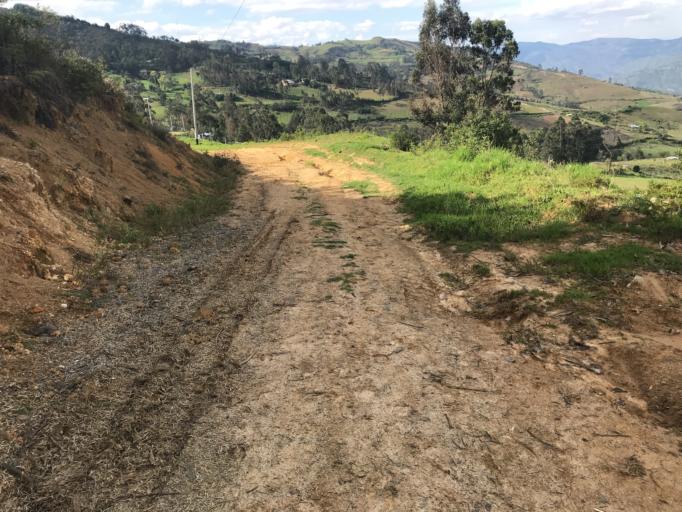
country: PE
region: Cajamarca
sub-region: Provincia de Chota
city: Querocoto
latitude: -6.3623
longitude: -79.0308
